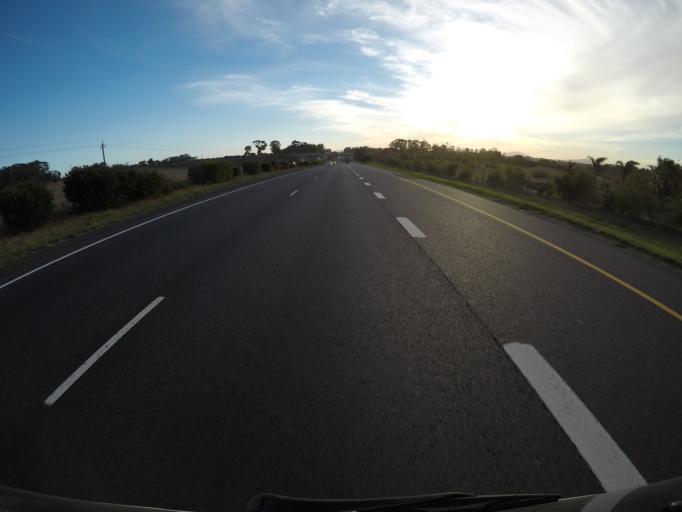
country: ZA
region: Western Cape
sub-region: City of Cape Town
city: Kraaifontein
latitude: -33.8186
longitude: 18.7956
